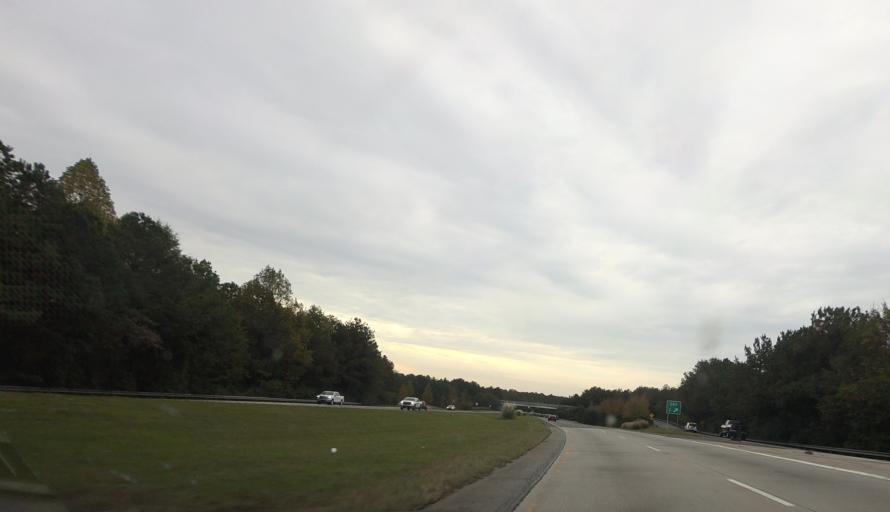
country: US
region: Alabama
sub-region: Russell County
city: Phenix City
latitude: 32.5157
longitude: -84.9928
